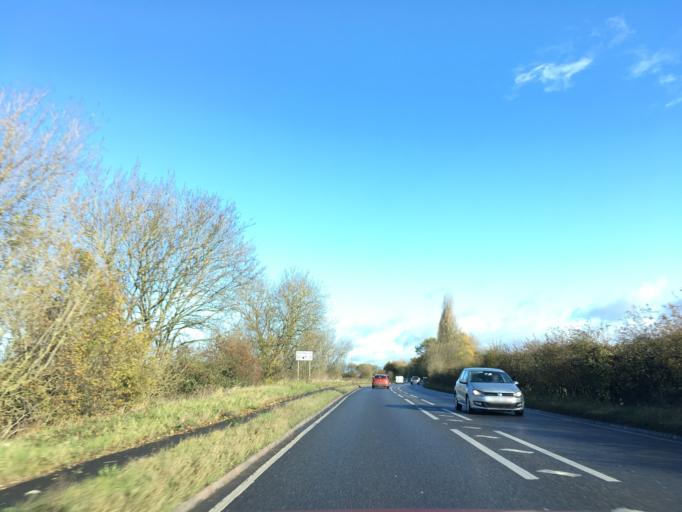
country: GB
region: England
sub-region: Gloucestershire
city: Gotherington
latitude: 52.0223
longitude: -2.0130
